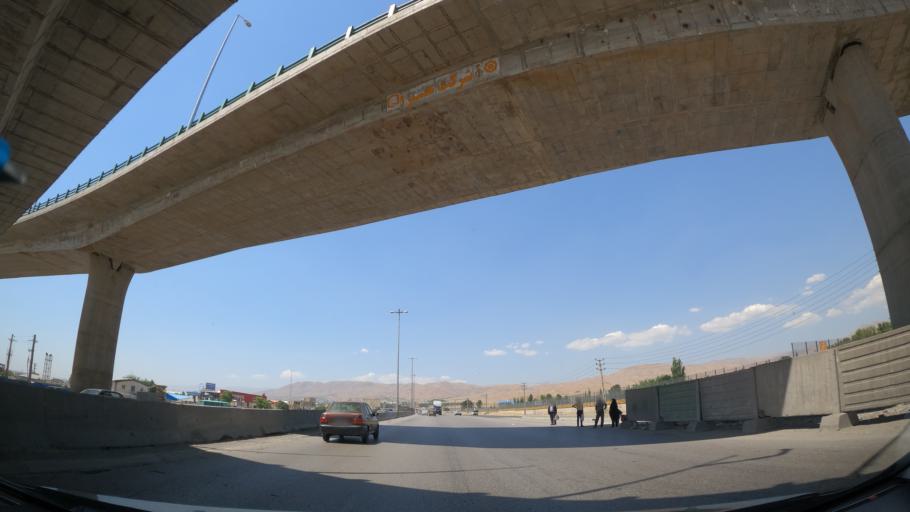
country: IR
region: Alborz
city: Karaj
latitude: 35.8506
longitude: 50.9091
